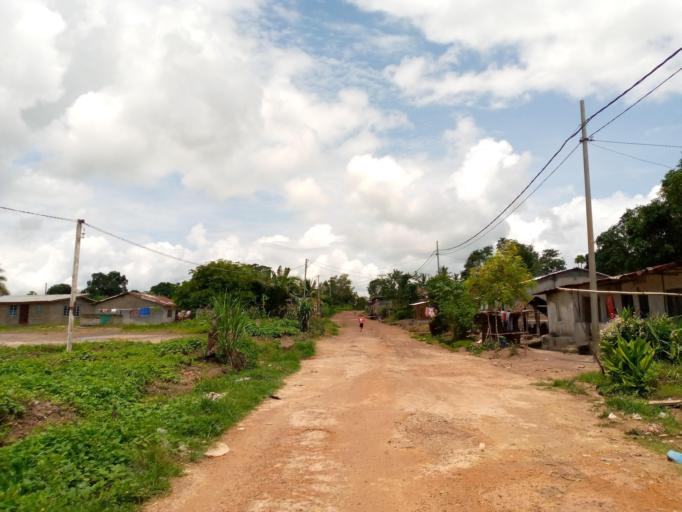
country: SL
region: Northern Province
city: Magburaka
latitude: 8.7184
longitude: -11.9488
